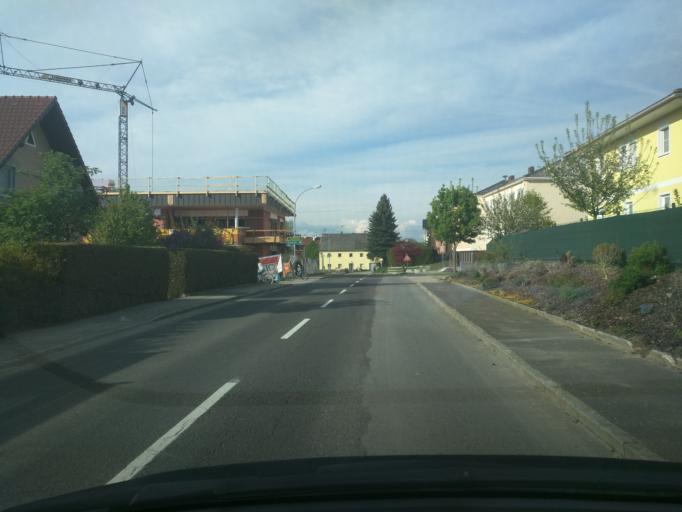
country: AT
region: Upper Austria
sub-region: Politischer Bezirk Kirchdorf an der Krems
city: Kremsmunster
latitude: 48.0957
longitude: 14.1111
